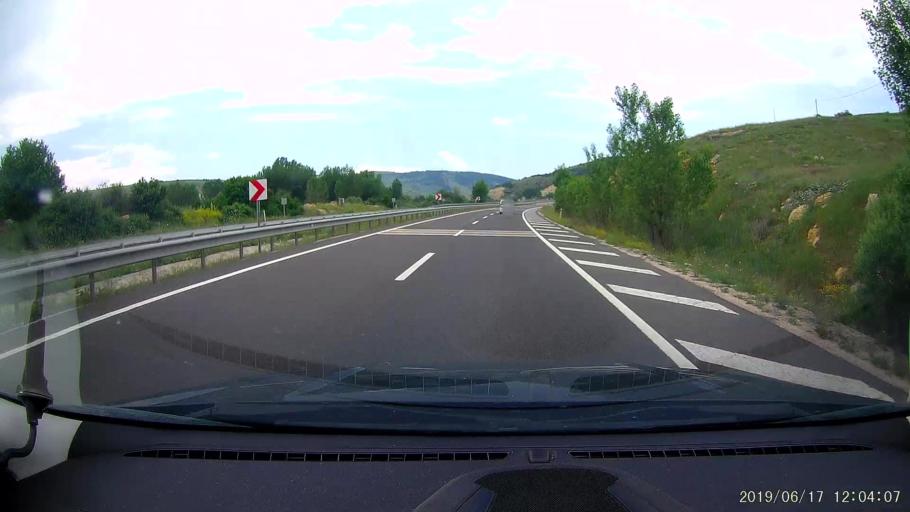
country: TR
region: Cankiri
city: Cerkes
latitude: 40.8248
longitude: 32.8076
